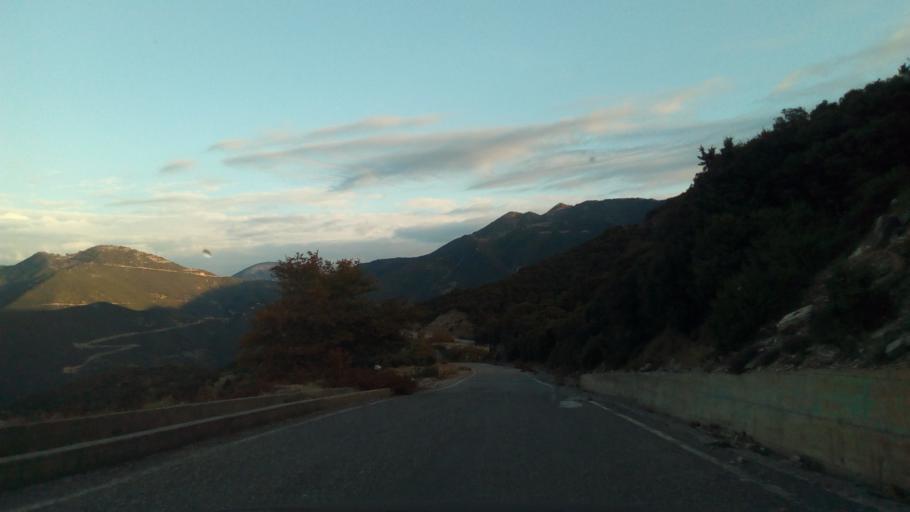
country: GR
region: West Greece
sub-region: Nomos Aitolias kai Akarnanias
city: Nafpaktos
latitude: 38.5031
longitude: 21.8362
